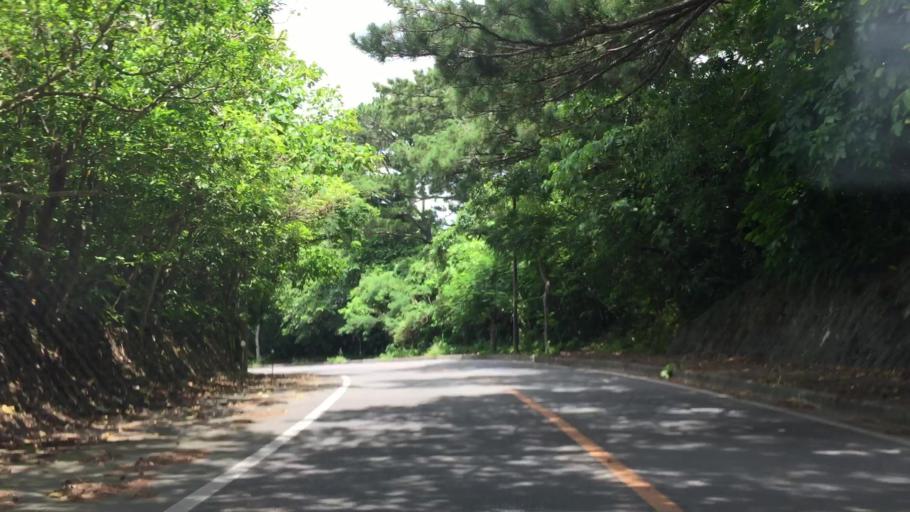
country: JP
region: Okinawa
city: Ishigaki
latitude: 24.3697
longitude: 124.1567
